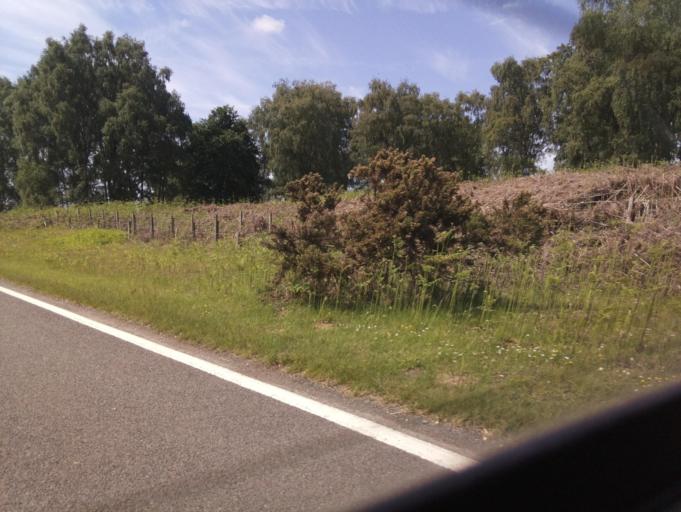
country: GB
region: England
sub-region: North Lincolnshire
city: Manton
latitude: 53.5255
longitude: -0.5792
